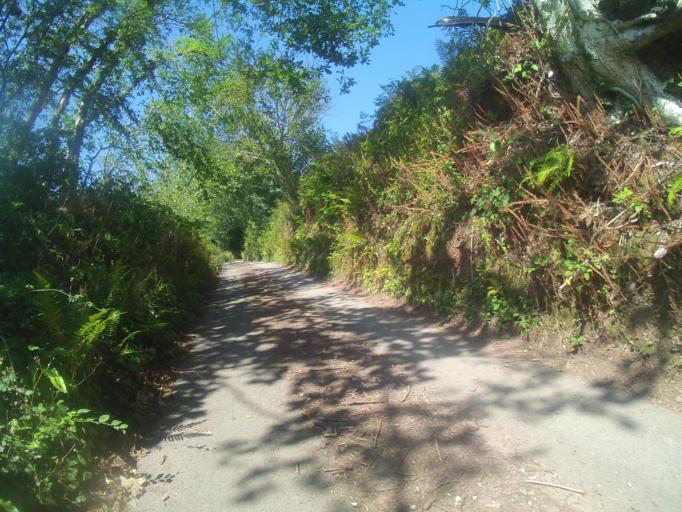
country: GB
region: England
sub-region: Devon
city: Dartmouth
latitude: 50.3597
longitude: -3.6183
